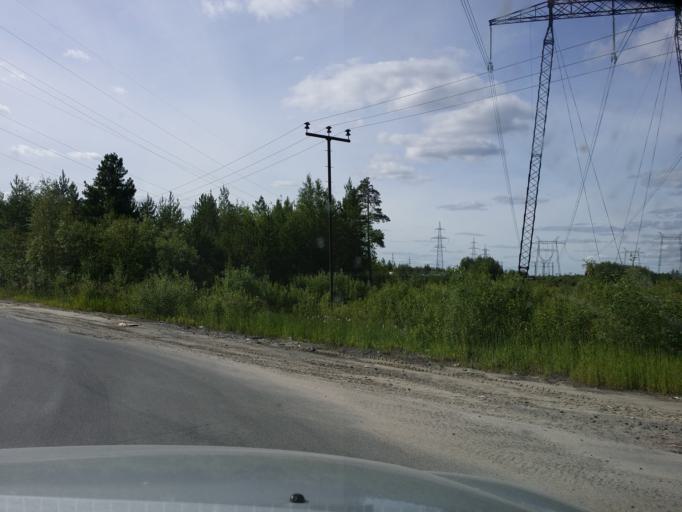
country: RU
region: Khanty-Mansiyskiy Avtonomnyy Okrug
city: Nizhnevartovsk
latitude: 60.9994
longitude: 76.5664
